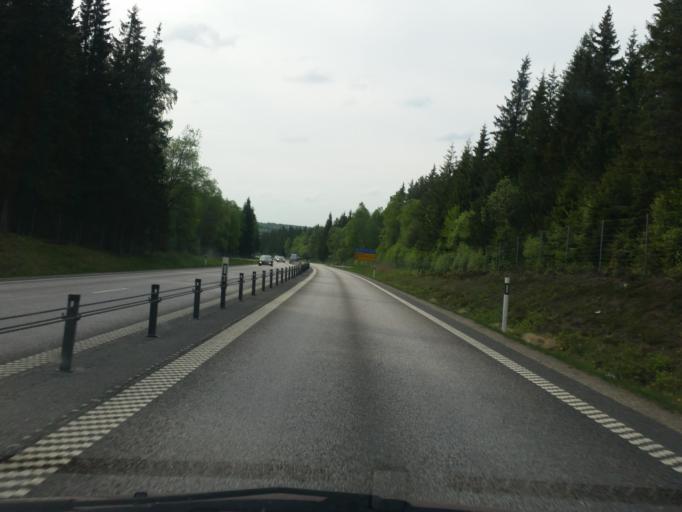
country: SE
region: Vaestra Goetaland
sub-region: Ulricehamns Kommun
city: Ulricehamn
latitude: 57.7942
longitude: 13.6214
